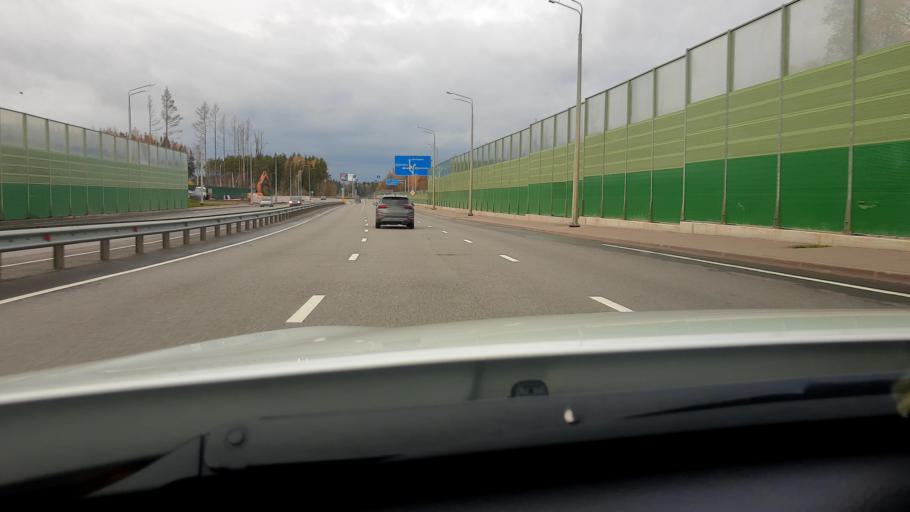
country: RU
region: Moskovskaya
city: Kokoshkino
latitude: 55.5513
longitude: 37.1580
